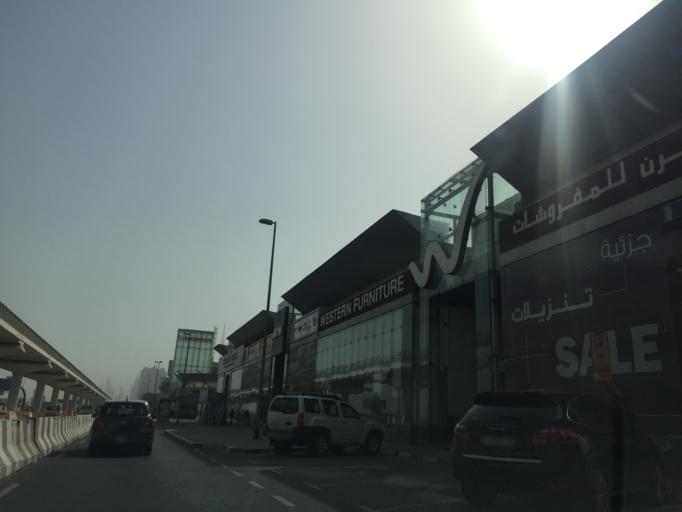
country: AE
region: Dubai
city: Dubai
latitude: 25.1668
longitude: 55.2381
